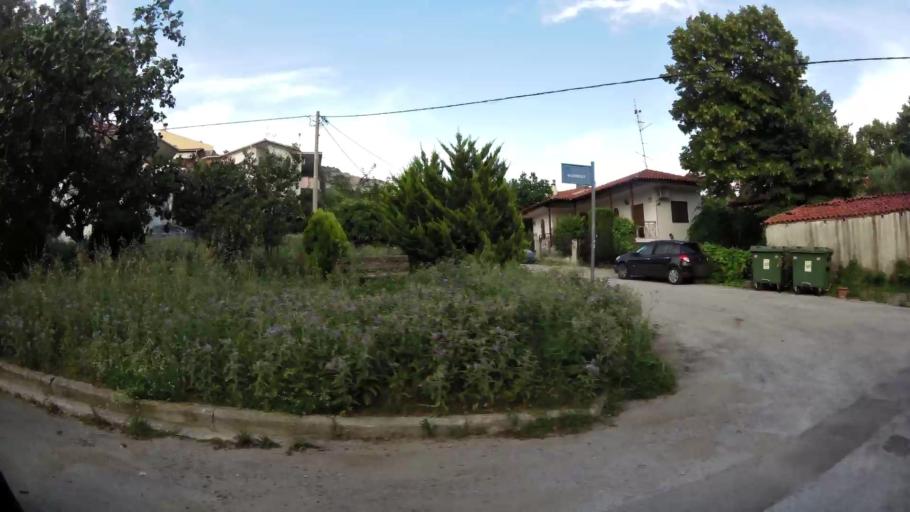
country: GR
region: Central Macedonia
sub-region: Nomos Thessalonikis
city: Pefka
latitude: 40.6521
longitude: 23.0000
